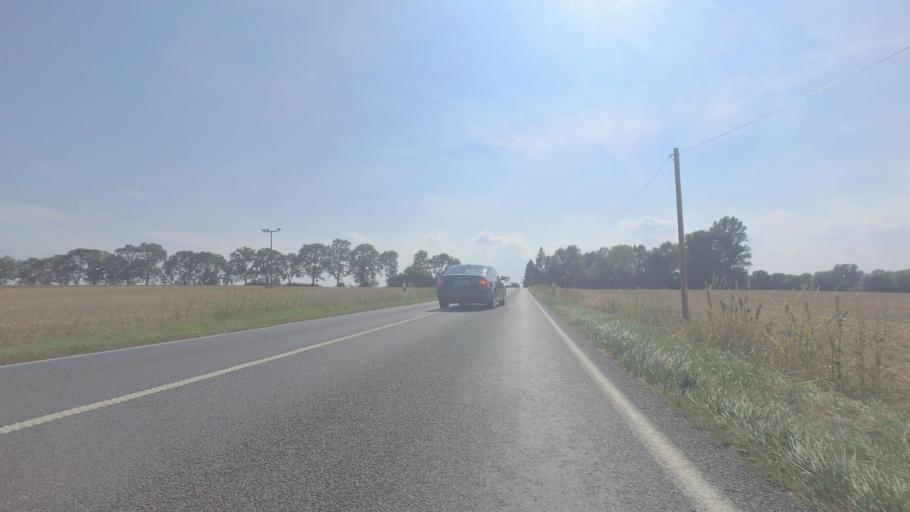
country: DE
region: Mecklenburg-Vorpommern
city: Brandshagen
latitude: 54.1522
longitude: 13.1593
